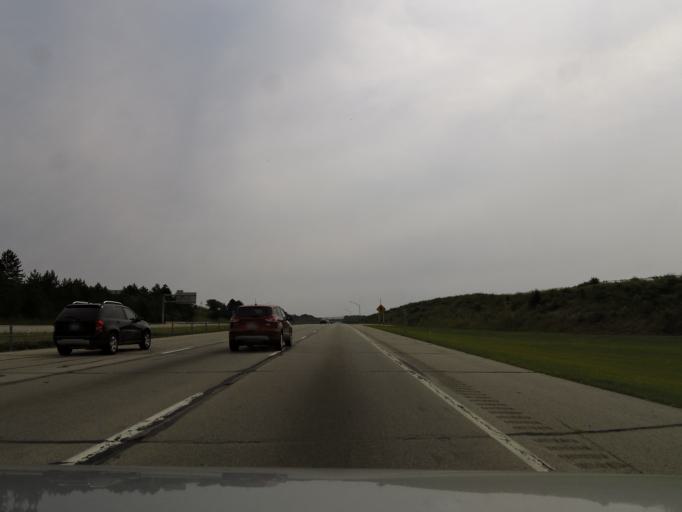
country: US
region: Ohio
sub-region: Montgomery County
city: Centerville
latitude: 39.6470
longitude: -84.1544
